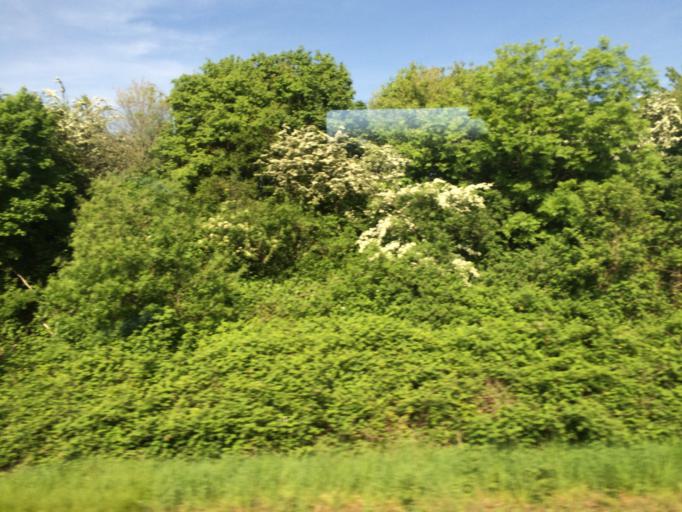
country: DE
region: North Rhine-Westphalia
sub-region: Regierungsbezirk Dusseldorf
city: Langenfeld
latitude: 51.1112
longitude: 6.9301
